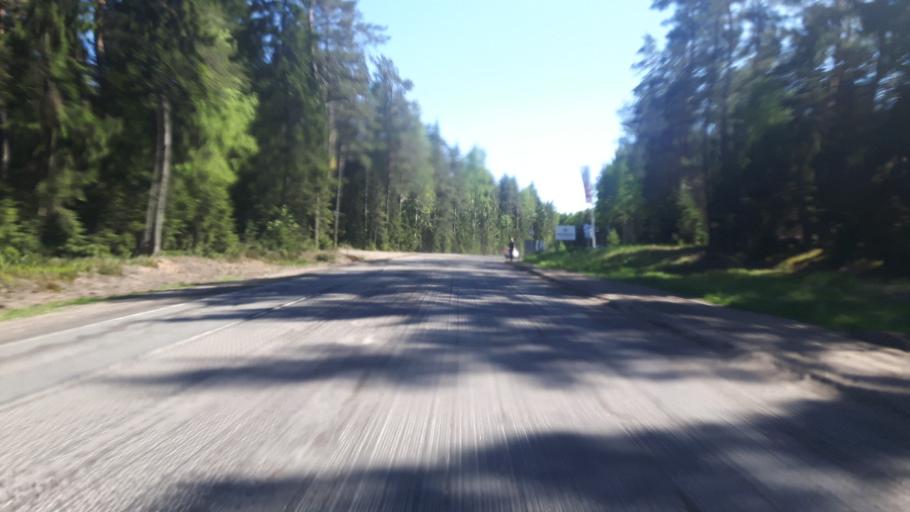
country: RU
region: Leningrad
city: Sosnovyy Bor
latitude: 60.2320
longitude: 29.0017
